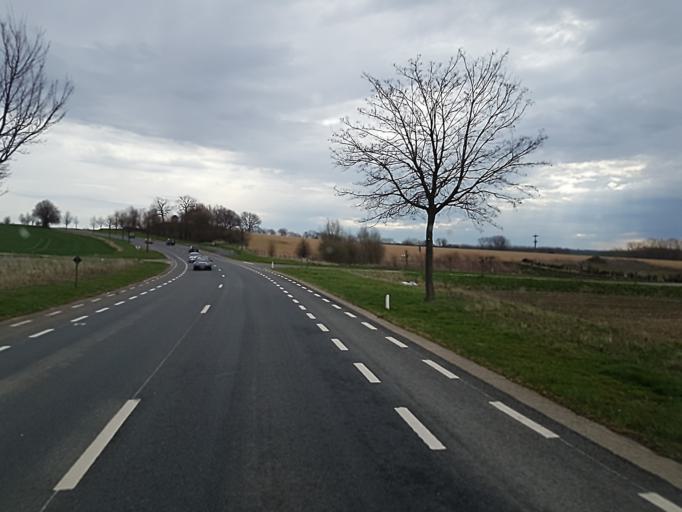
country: BE
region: Wallonia
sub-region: Province de Liege
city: Oreye
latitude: 50.7364
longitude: 5.3637
